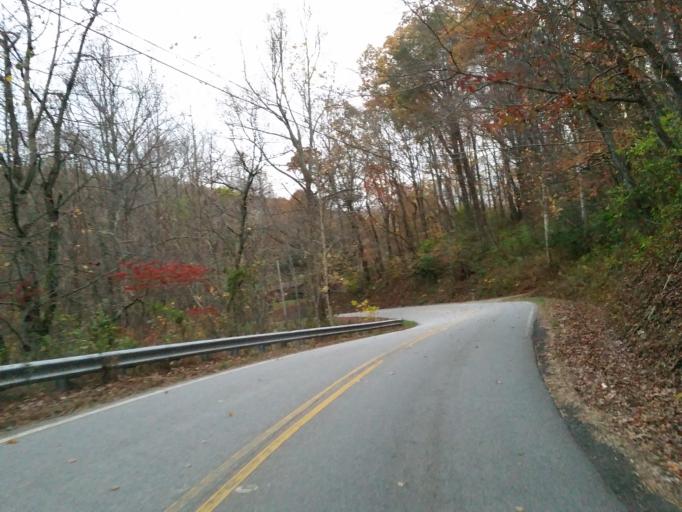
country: US
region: Georgia
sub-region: Lumpkin County
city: Dahlonega
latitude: 34.7027
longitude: -84.0520
